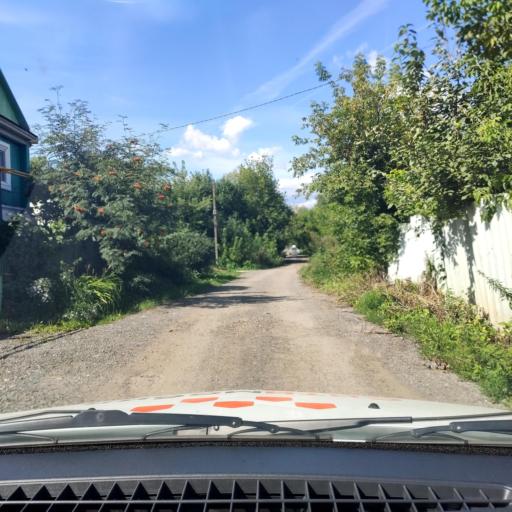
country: RU
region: Bashkortostan
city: Ufa
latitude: 54.7101
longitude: 55.9325
